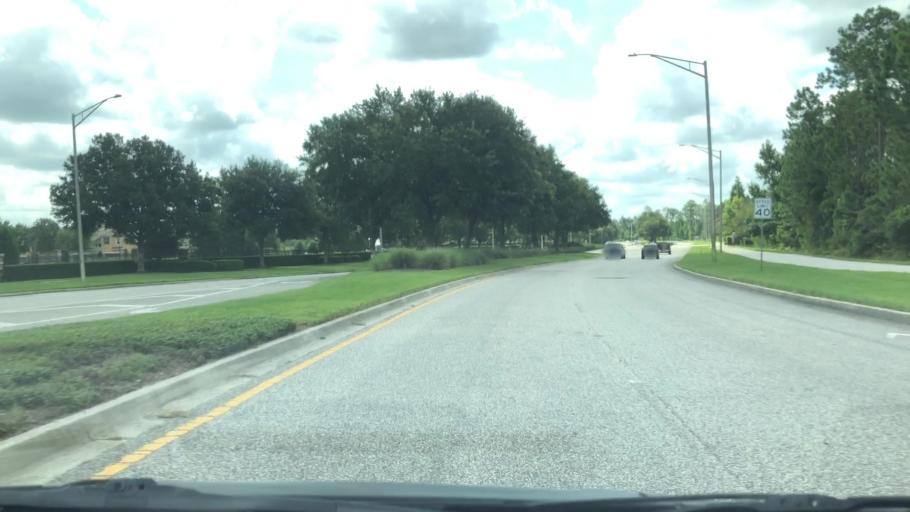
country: US
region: Florida
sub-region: Saint Johns County
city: Fruit Cove
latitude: 30.1346
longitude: -81.5446
